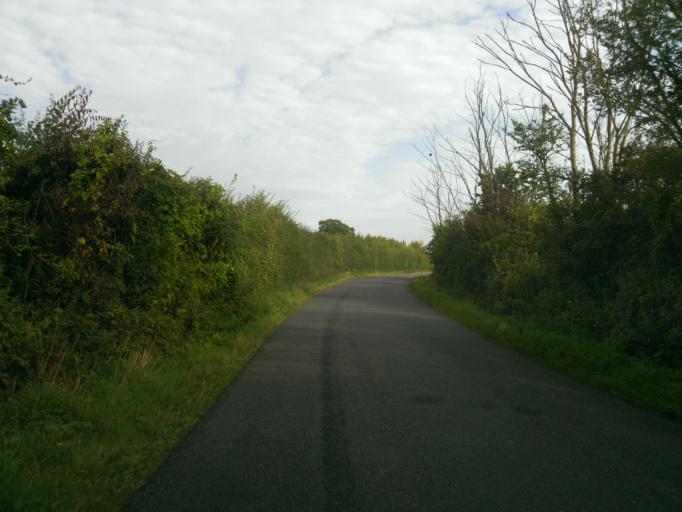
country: GB
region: England
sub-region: Essex
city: Saint Osyth
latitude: 51.8259
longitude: 1.1022
